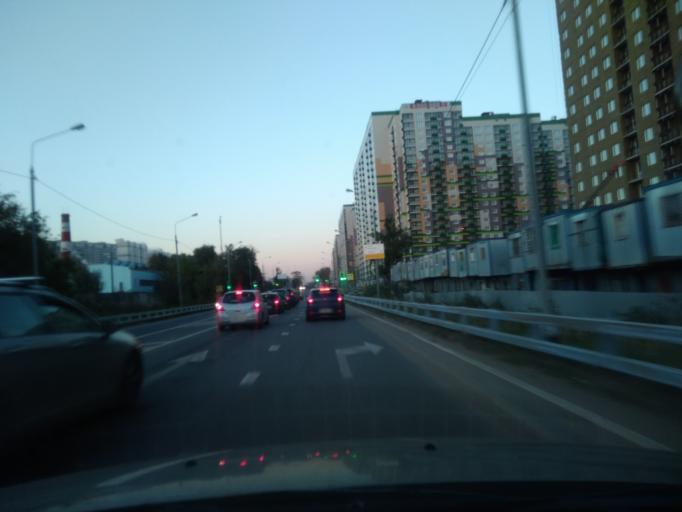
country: RU
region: Moscow
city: Khimki
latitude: 55.8665
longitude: 37.3941
